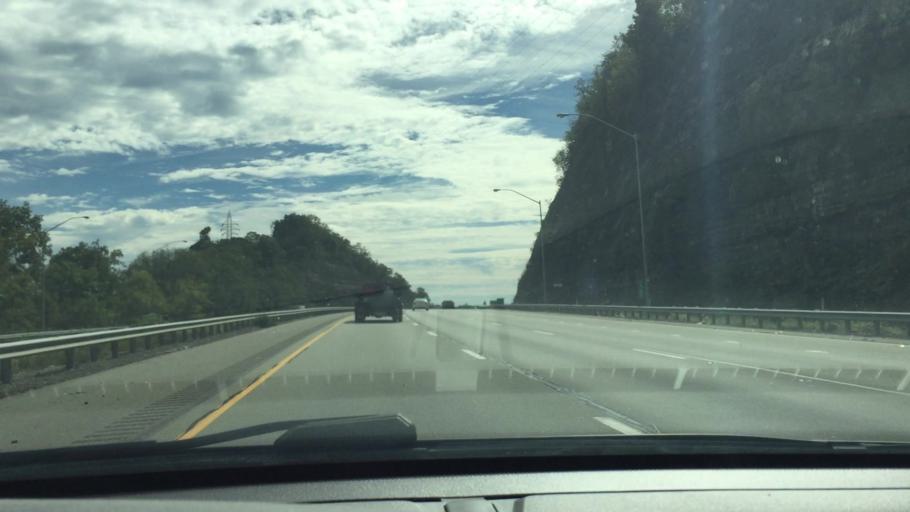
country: US
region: Pennsylvania
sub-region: Allegheny County
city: Heidelberg
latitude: 40.3948
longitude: -80.1021
